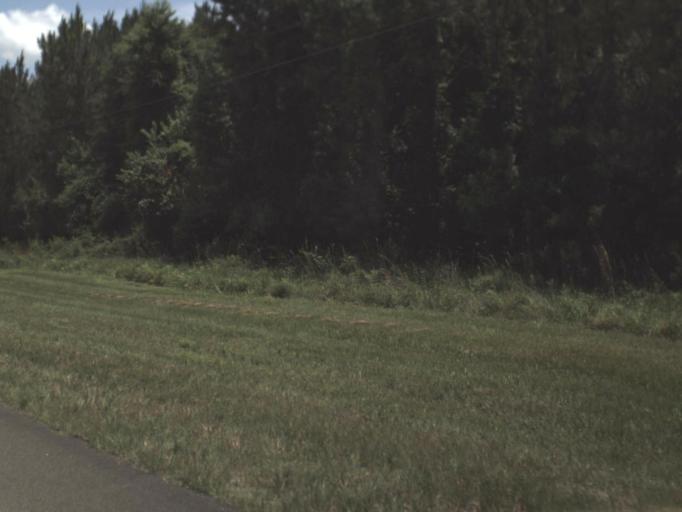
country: US
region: Florida
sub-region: Alachua County
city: Alachua
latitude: 29.8852
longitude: -82.4232
